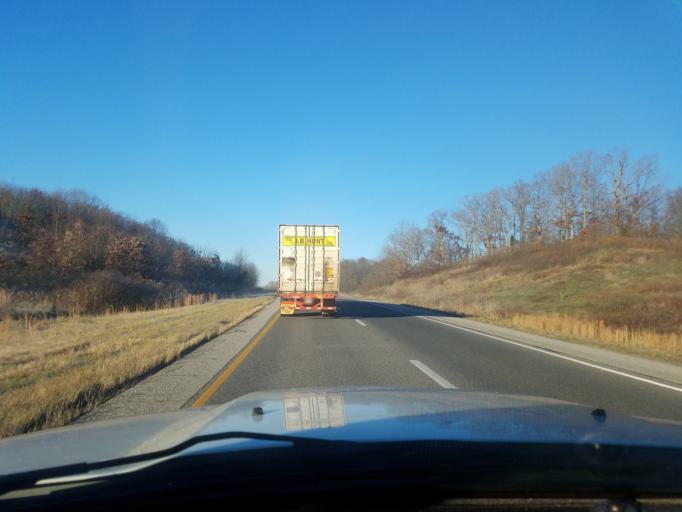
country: US
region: Indiana
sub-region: Dubois County
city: Ferdinand
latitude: 38.2129
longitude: -86.7595
